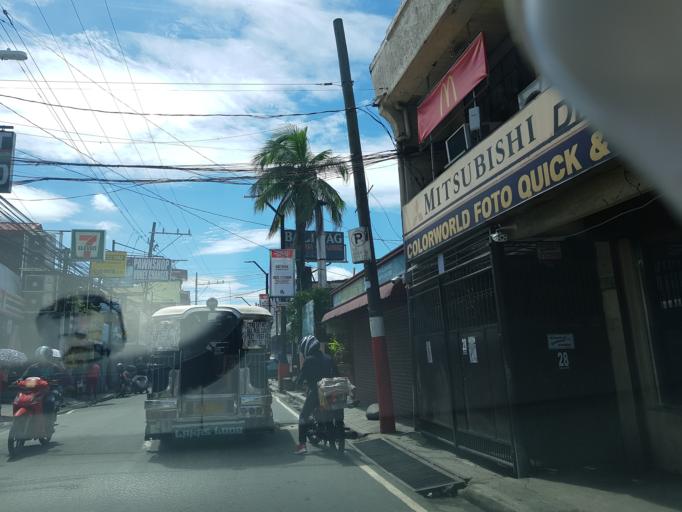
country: PH
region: Calabarzon
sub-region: Province of Rizal
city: Taguig
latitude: 14.5289
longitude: 121.0707
